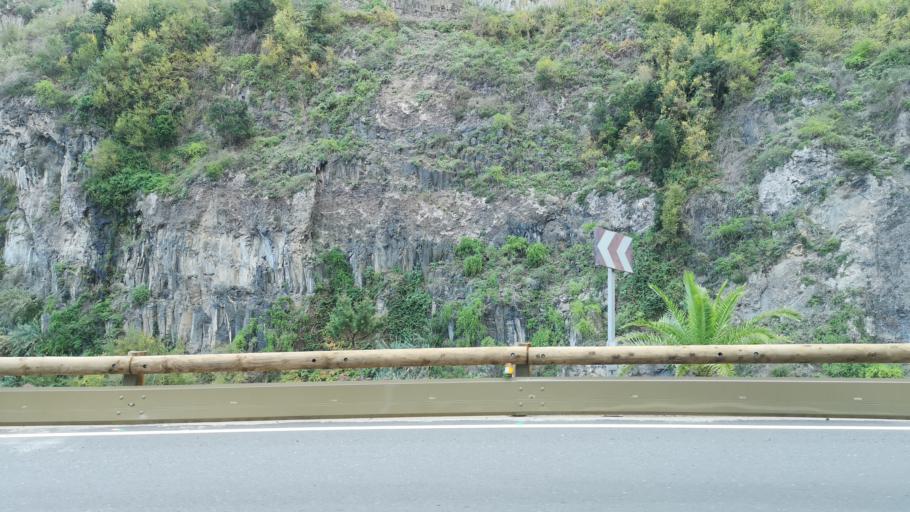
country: ES
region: Canary Islands
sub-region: Provincia de Santa Cruz de Tenerife
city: Agulo
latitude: 28.1849
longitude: -17.1954
